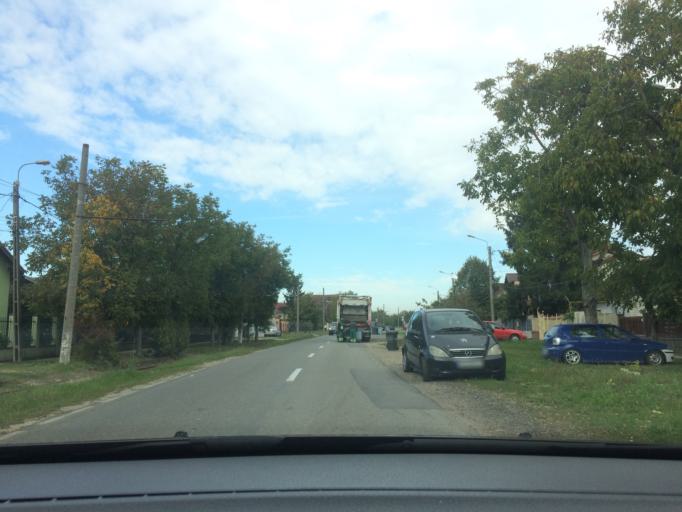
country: RO
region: Timis
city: Timisoara
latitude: 45.7542
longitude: 21.1910
